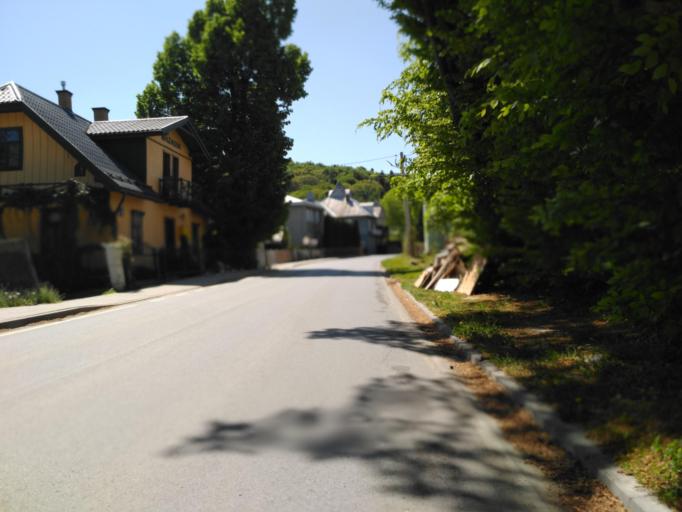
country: PL
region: Subcarpathian Voivodeship
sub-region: Powiat krosnienski
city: Iwonicz-Zdroj
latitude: 49.5684
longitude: 21.7932
